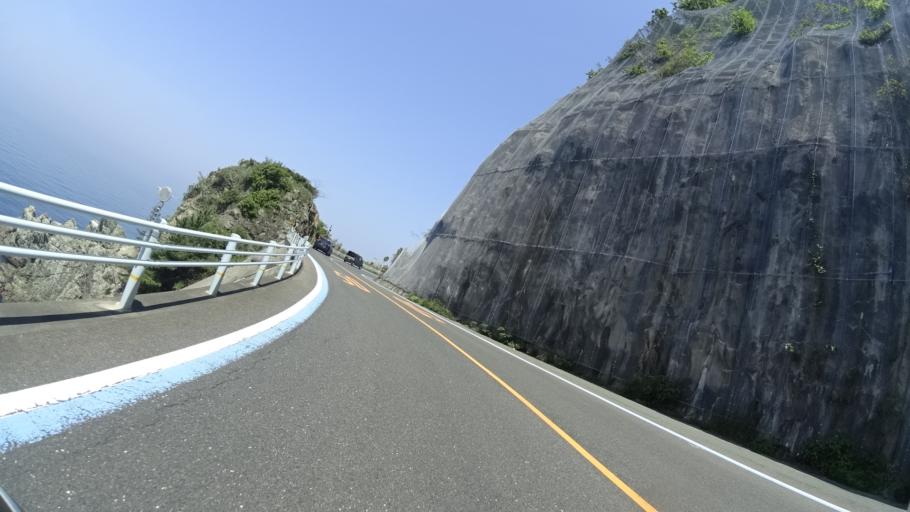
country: JP
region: Ehime
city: Ozu
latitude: 33.5943
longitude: 132.4576
